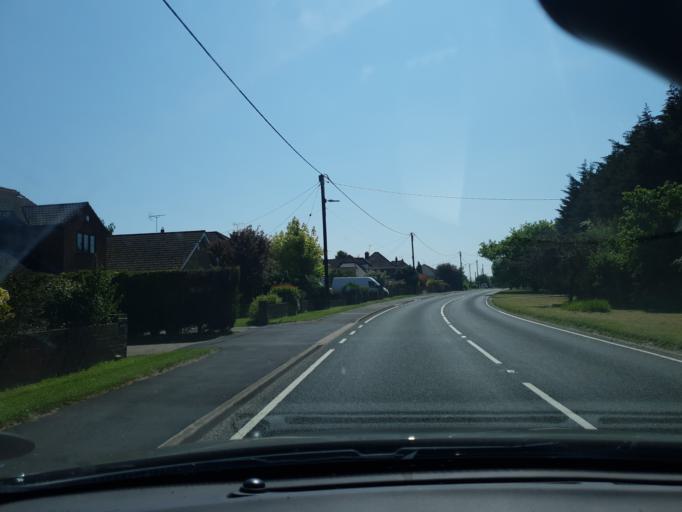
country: GB
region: England
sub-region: Essex
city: Great Bentley
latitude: 51.8454
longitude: 1.0334
